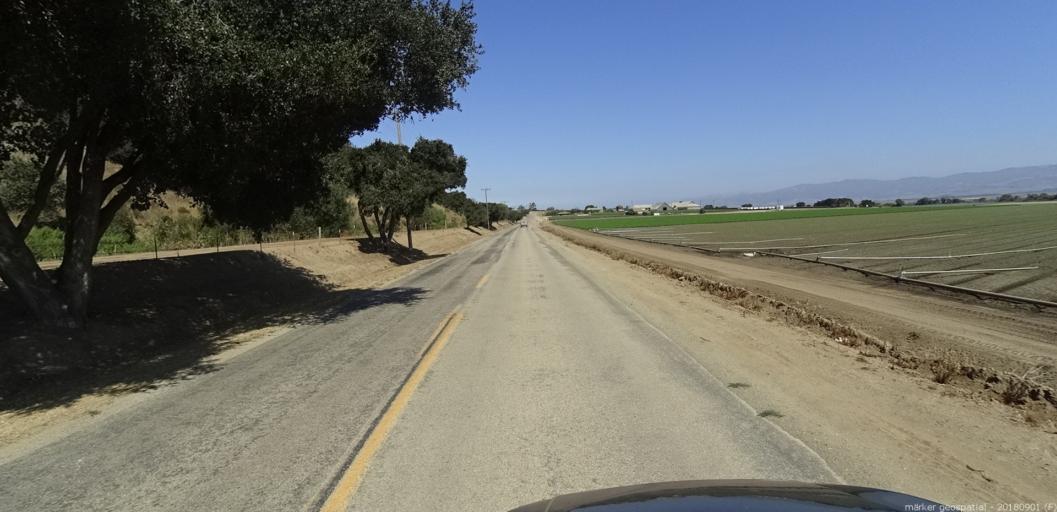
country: US
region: California
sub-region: Monterey County
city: Chualar
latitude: 36.5122
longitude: -121.5173
